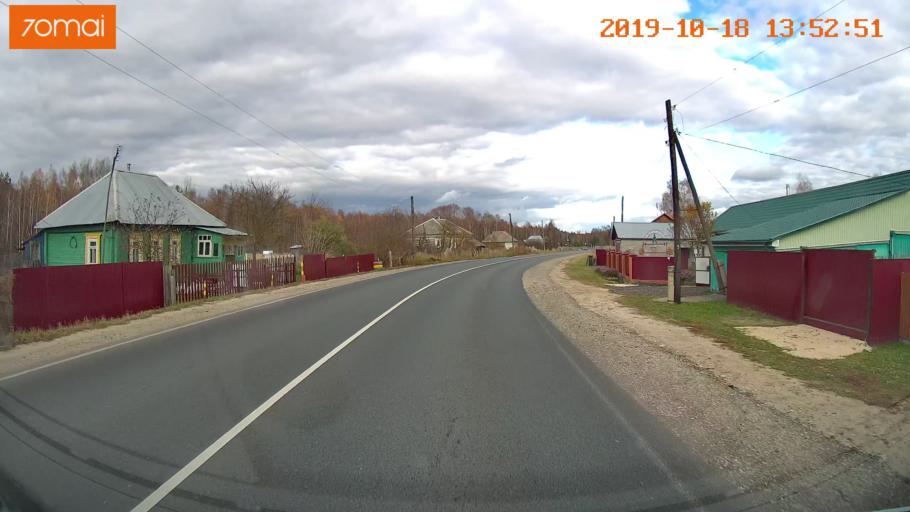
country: RU
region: Moskovskaya
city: Radovitskiy
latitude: 55.0330
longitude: 39.9714
